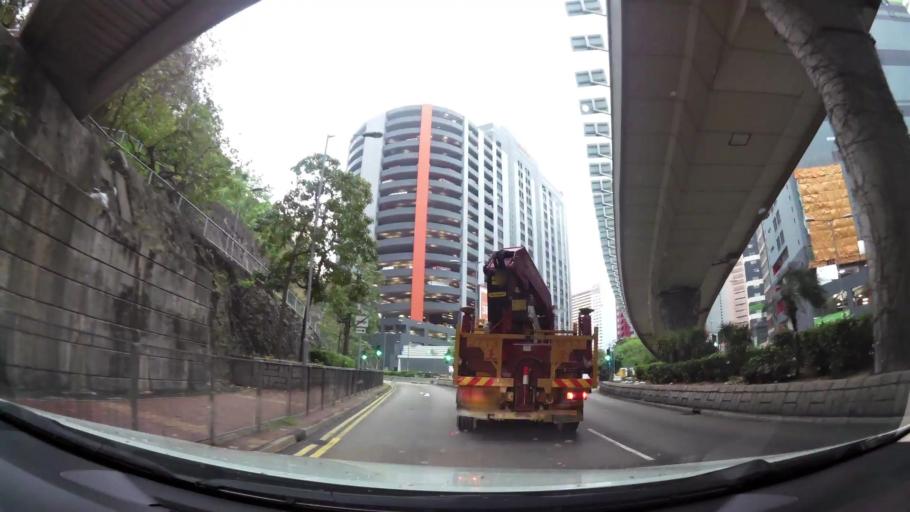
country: HK
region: Tsuen Wan
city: Tsuen Wan
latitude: 22.3658
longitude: 114.1212
